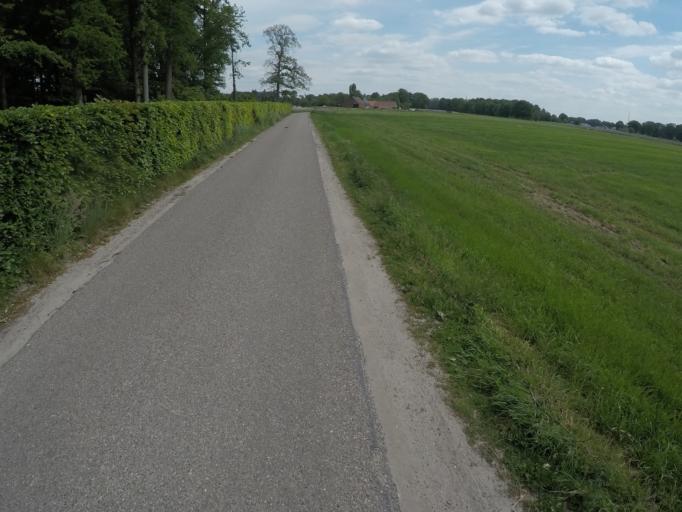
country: BE
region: Flanders
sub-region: Provincie Antwerpen
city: Oostmalle
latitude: 51.3069
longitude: 4.6985
